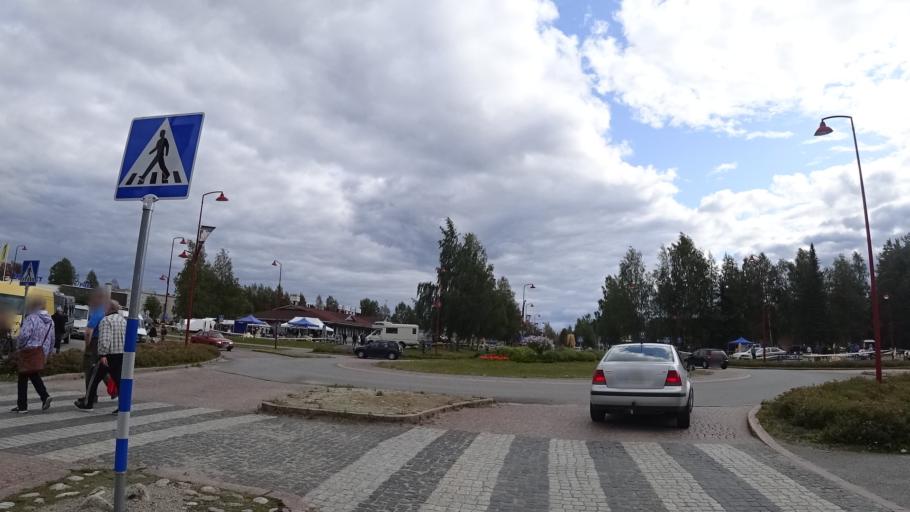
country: FI
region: North Karelia
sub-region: Joensuu
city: Ilomantsi
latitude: 62.6718
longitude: 30.9323
